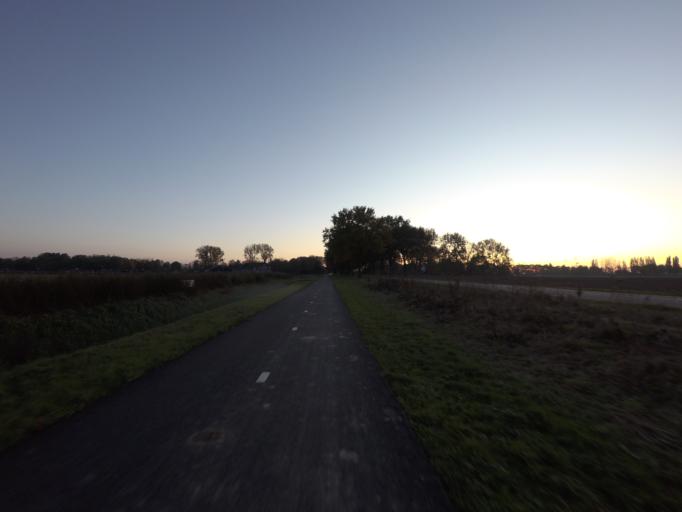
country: NL
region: North Brabant
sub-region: Gemeente Woudrichem
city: Almkerk
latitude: 51.7851
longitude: 4.9654
